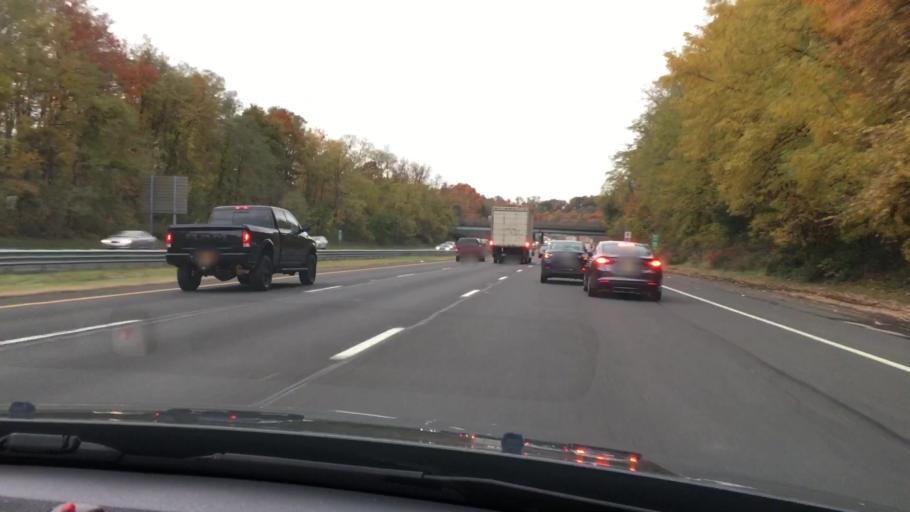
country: US
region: New Jersey
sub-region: Somerset County
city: Bernardsville
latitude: 40.7235
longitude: -74.5450
